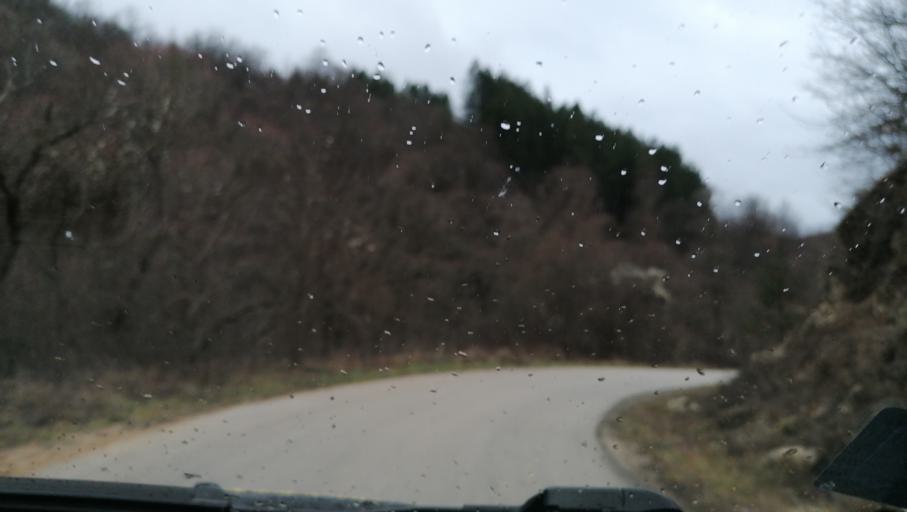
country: RS
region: Central Serbia
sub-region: Pirotski Okrug
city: Dimitrovgrad
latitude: 42.9783
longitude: 22.6507
